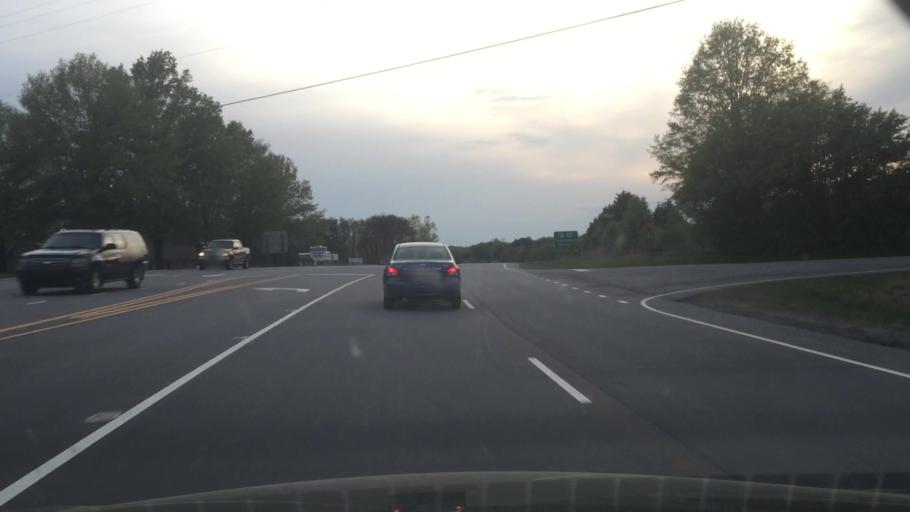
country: US
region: North Carolina
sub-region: Rockingham County
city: Reidsville
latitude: 36.3132
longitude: -79.6320
